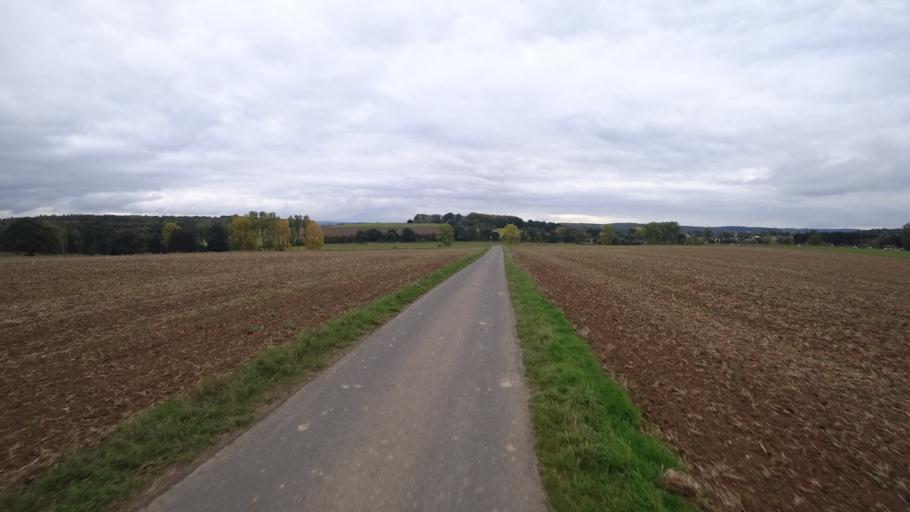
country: DE
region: Rheinland-Pfalz
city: Marienhausen
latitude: 50.5461
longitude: 7.6935
